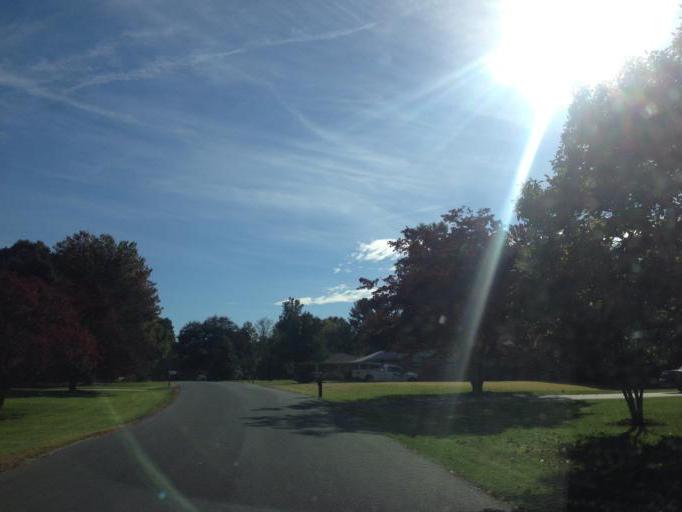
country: US
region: Maryland
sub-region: Howard County
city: Columbia
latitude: 39.2767
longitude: -76.8504
